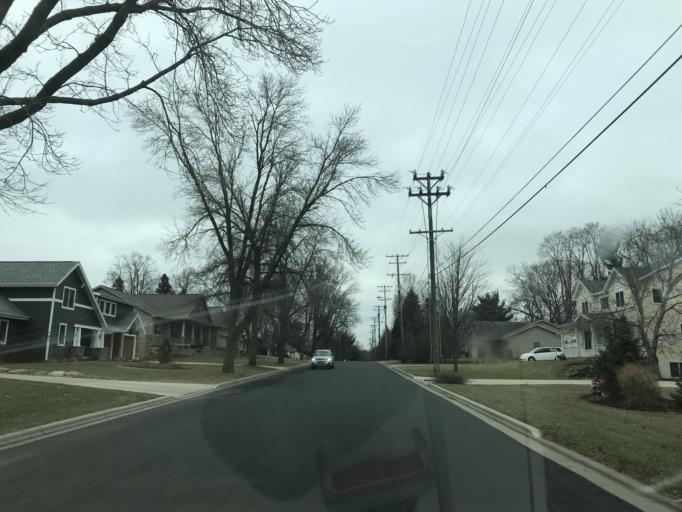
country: US
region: Wisconsin
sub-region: Dane County
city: Monona
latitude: 43.0648
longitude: -89.3335
